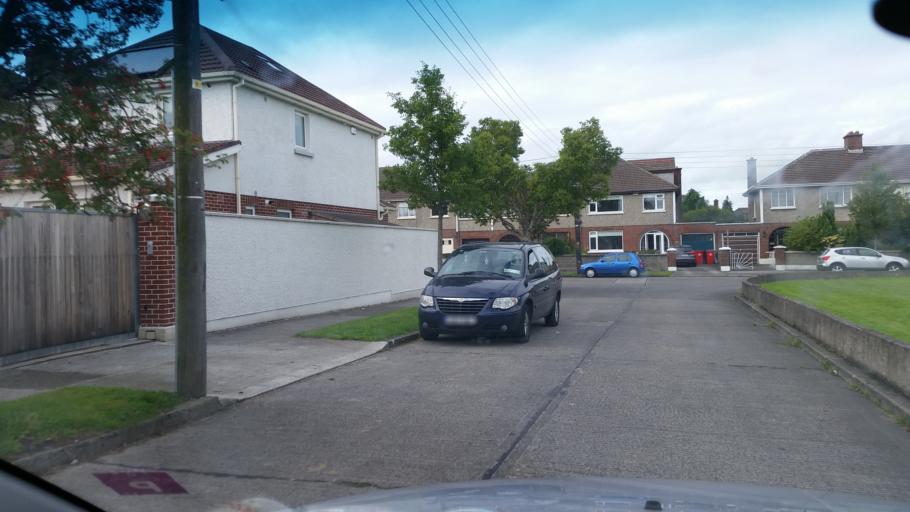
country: IE
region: Leinster
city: Ballymun
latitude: 53.3888
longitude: -6.2741
